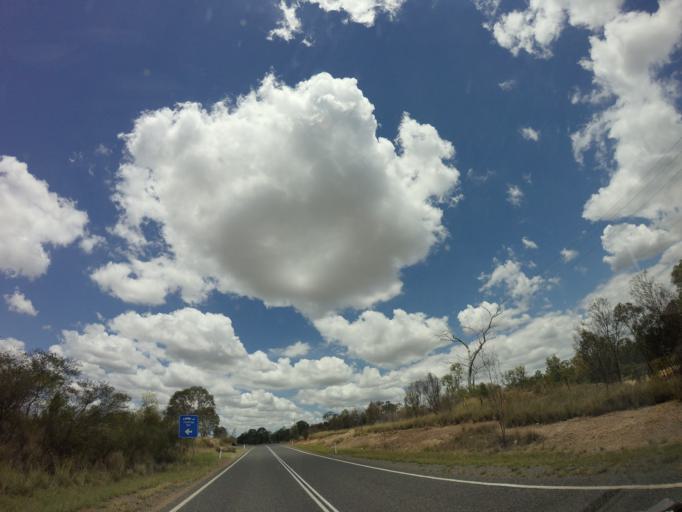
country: AU
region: Queensland
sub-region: Western Downs
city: Dalby
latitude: -27.9755
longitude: 151.0989
